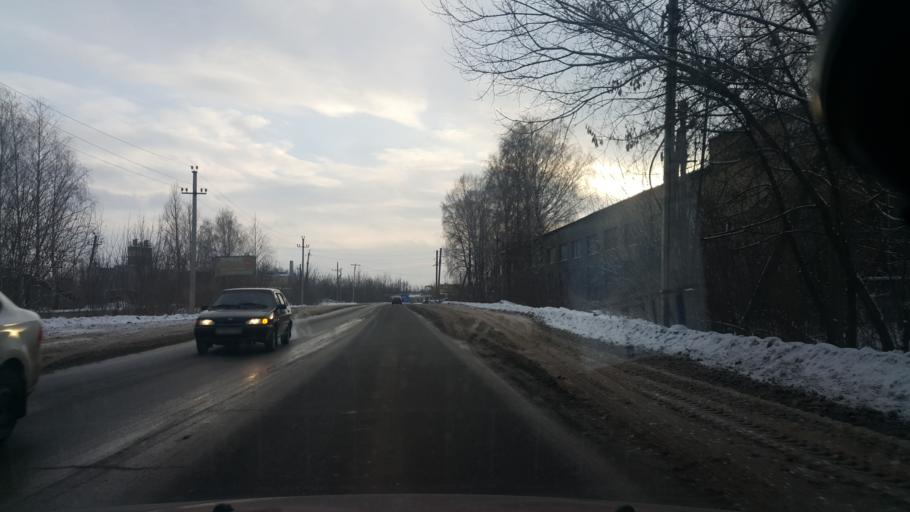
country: RU
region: Tambov
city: Pokrovo-Prigorodnoye
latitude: 52.6569
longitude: 41.4229
